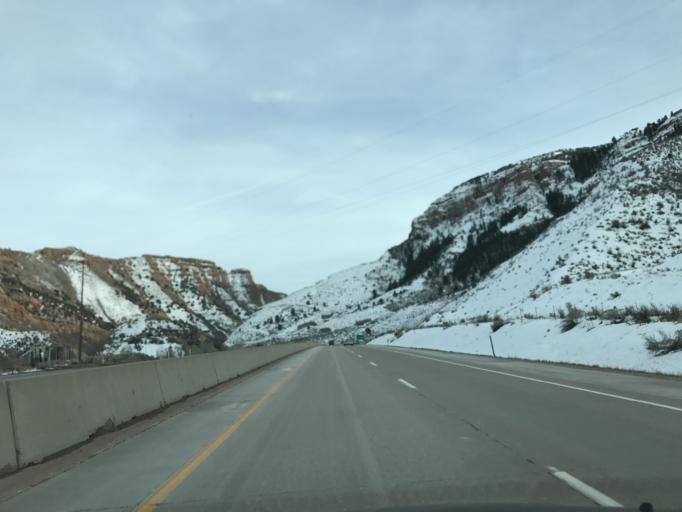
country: US
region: Utah
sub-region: Morgan County
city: Morgan
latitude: 41.0610
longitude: -111.5430
